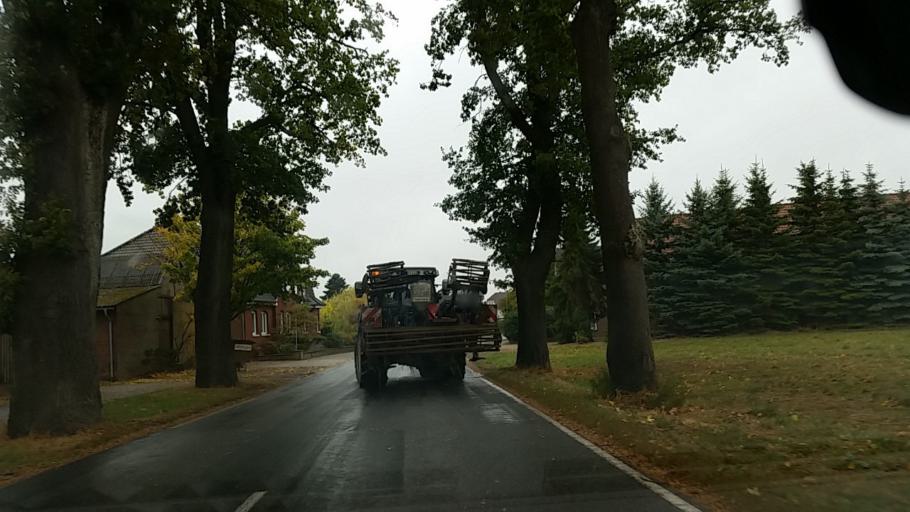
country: DE
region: Lower Saxony
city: Wittingen
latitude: 52.7082
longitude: 10.7715
